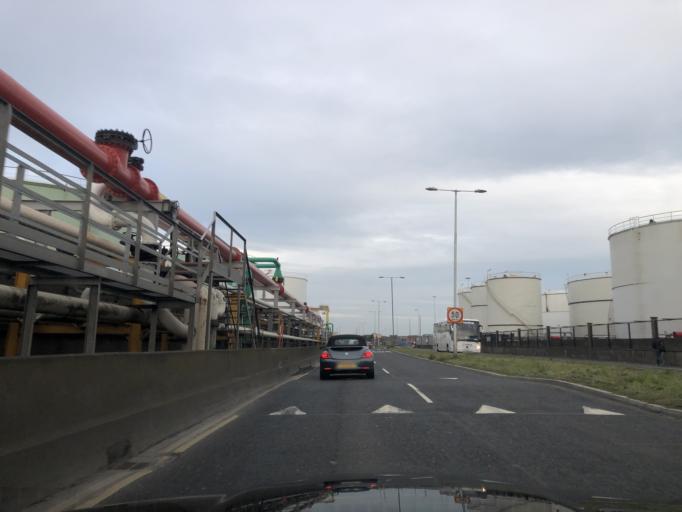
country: IE
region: Leinster
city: Sandymount
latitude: 53.3515
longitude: -6.2057
